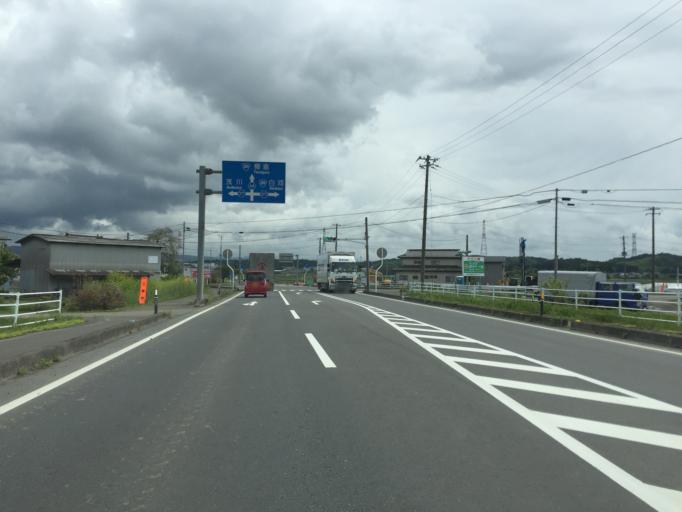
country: JP
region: Fukushima
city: Ishikawa
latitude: 37.0683
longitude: 140.3694
